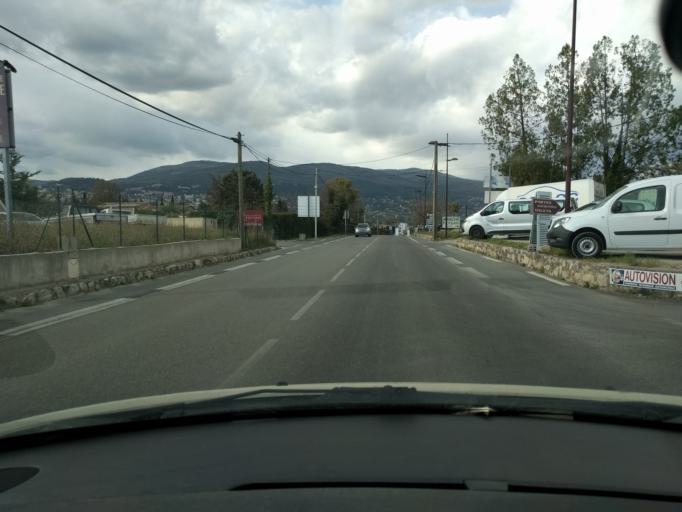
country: FR
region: Provence-Alpes-Cote d'Azur
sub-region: Departement des Alpes-Maritimes
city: Mouans-Sartoux
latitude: 43.6338
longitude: 6.9574
